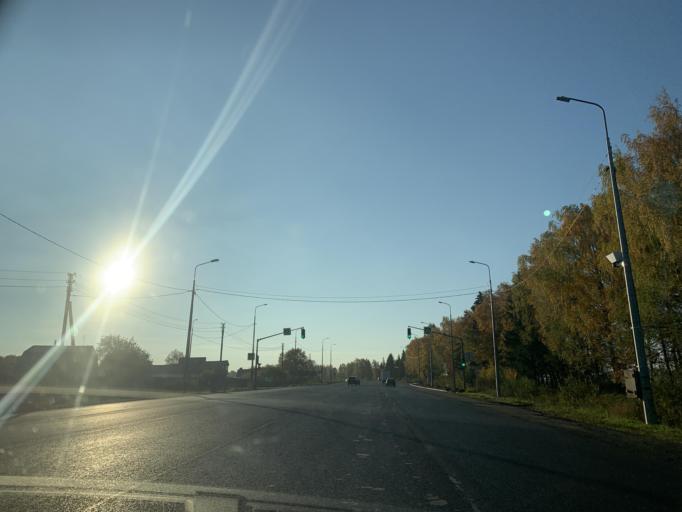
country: RU
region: Jaroslavl
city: Konstantinovskiy
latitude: 57.7899
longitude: 39.6084
